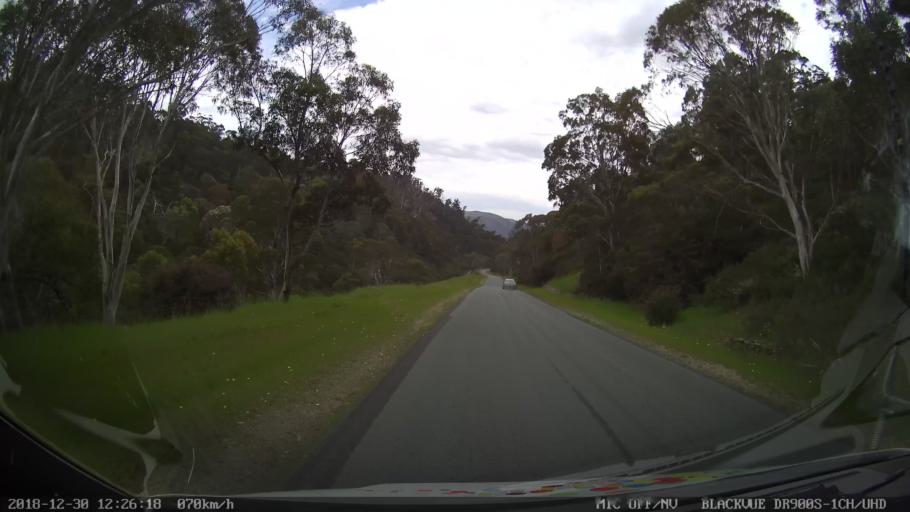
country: AU
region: New South Wales
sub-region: Snowy River
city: Jindabyne
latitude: -36.3406
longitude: 148.4892
